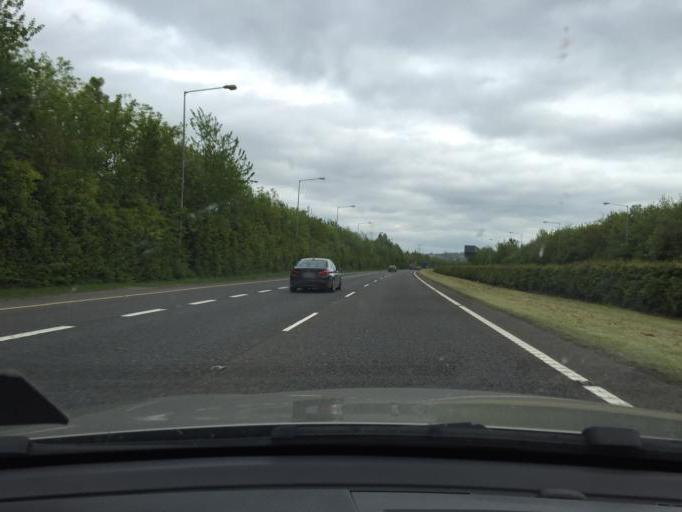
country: IE
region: Leinster
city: Balrothery
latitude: 53.5945
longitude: -6.2165
